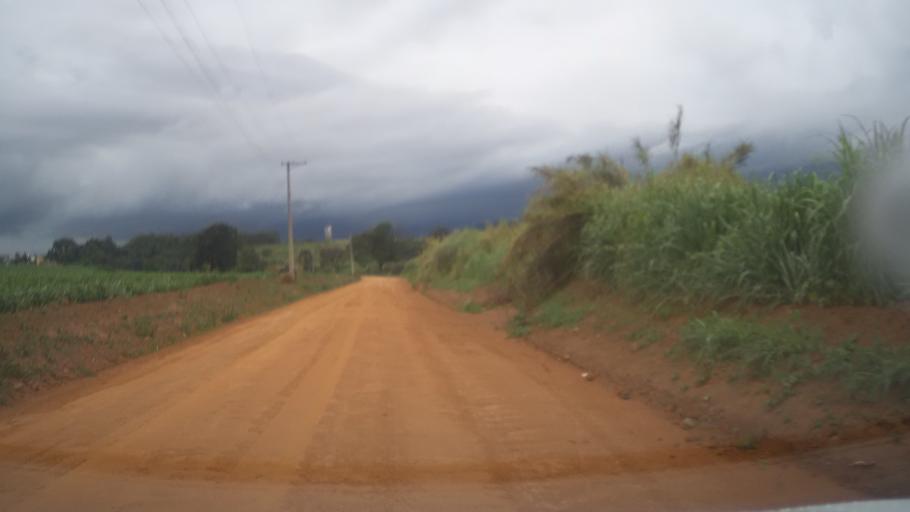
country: BR
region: Sao Paulo
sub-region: Itupeva
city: Itupeva
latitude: -23.1804
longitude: -47.0561
